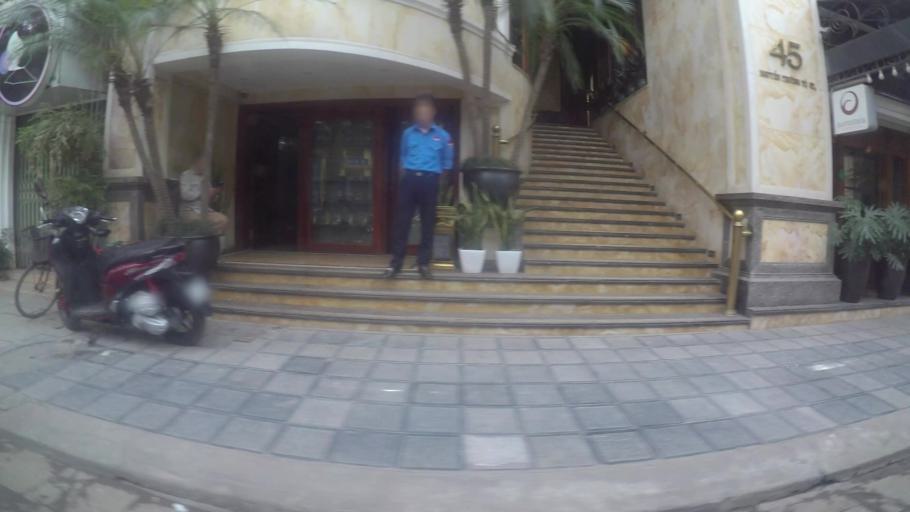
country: VN
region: Ha Noi
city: Hoan Kiem
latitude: 21.0423
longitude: 105.8458
